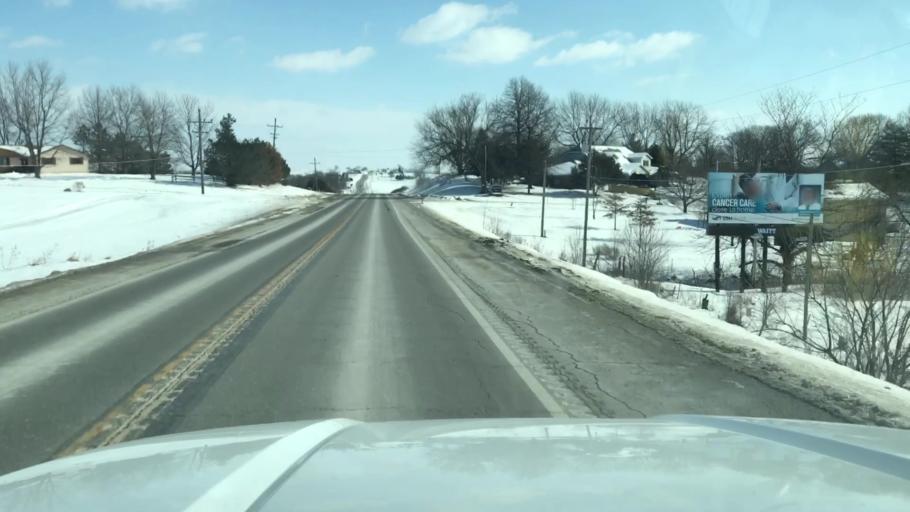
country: US
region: Missouri
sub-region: Nodaway County
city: Maryville
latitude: 40.3445
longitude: -94.7917
